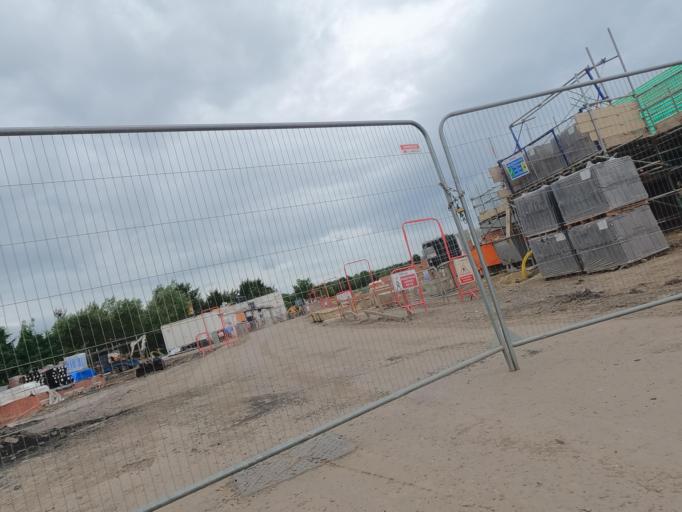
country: GB
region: England
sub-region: Northumberland
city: Blyth
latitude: 55.1120
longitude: -1.5395
